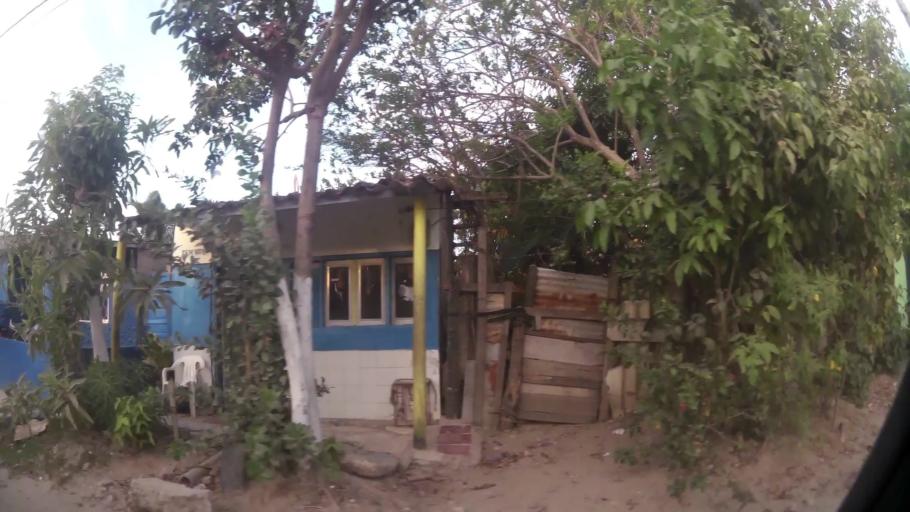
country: CO
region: Atlantico
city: Barranquilla
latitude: 10.9526
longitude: -74.8295
